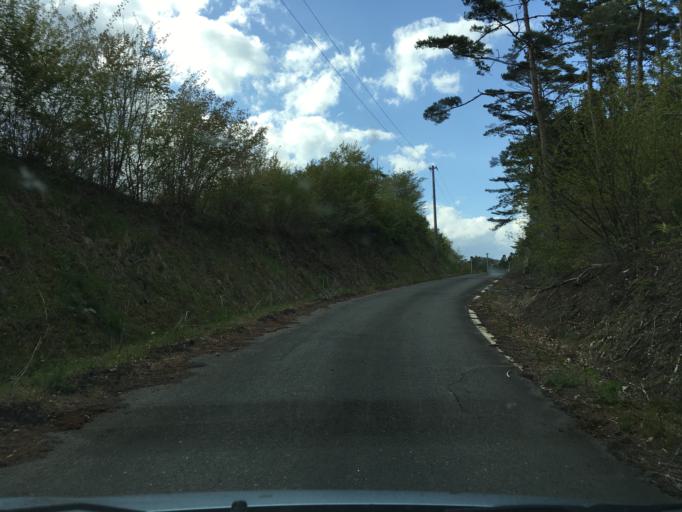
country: JP
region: Iwate
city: Ichinoseki
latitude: 38.7979
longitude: 141.4132
